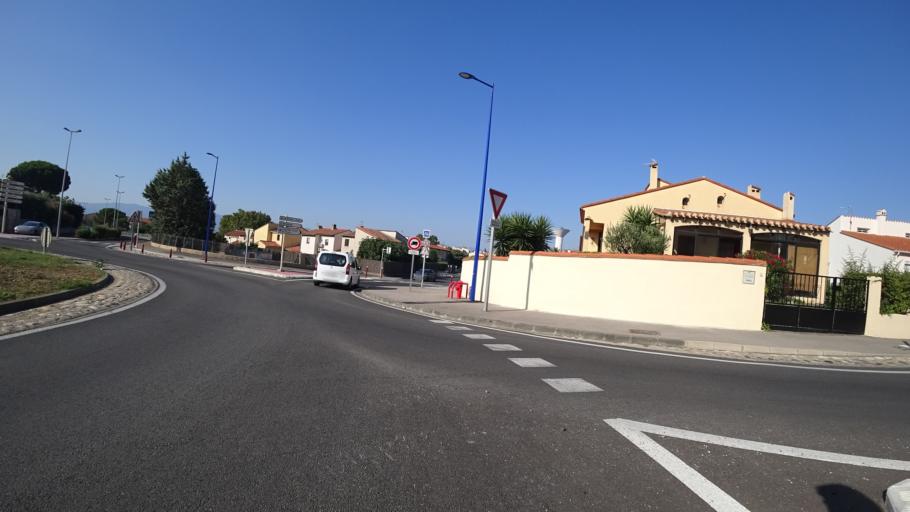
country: FR
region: Languedoc-Roussillon
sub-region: Departement des Pyrenees-Orientales
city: Cabestany
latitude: 42.6831
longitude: 2.9437
